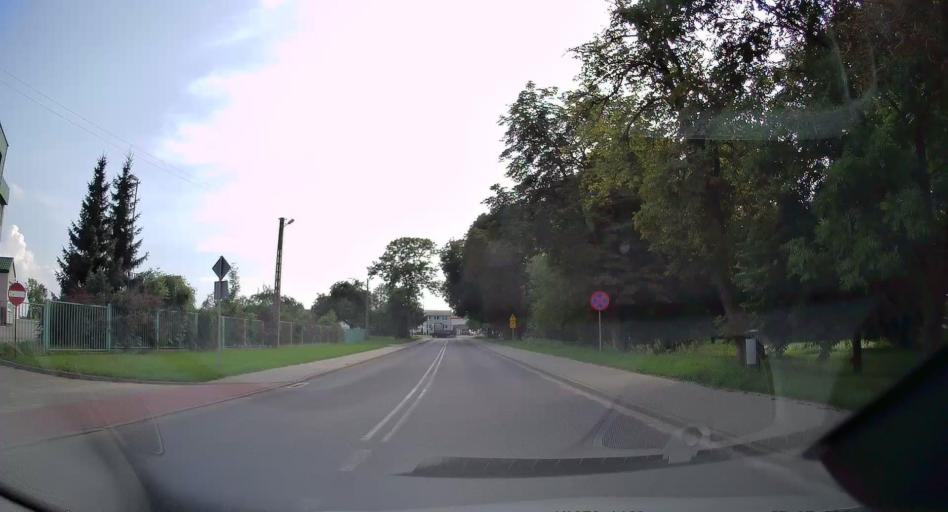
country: PL
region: Lodz Voivodeship
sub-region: Powiat tomaszowski
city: Rzeczyca
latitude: 51.5978
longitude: 20.2933
